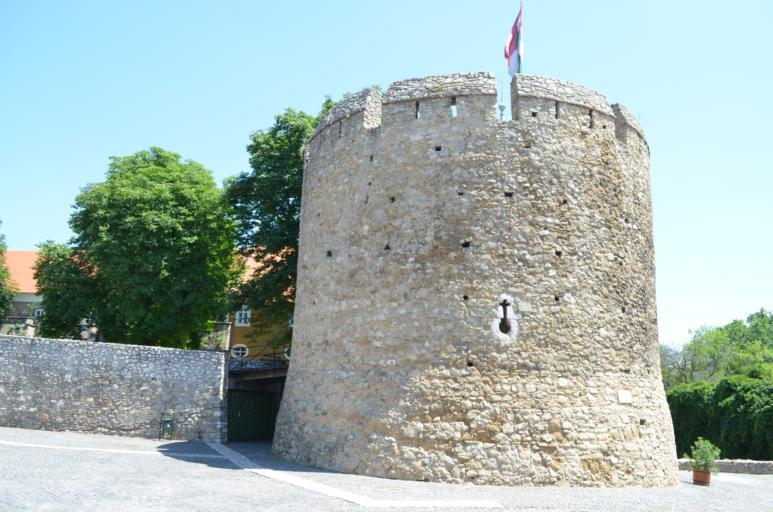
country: HU
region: Baranya
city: Pecs
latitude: 46.0778
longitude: 18.2213
